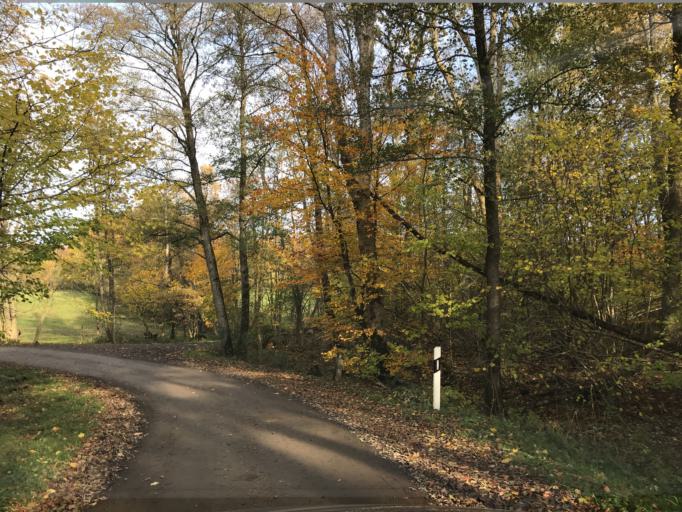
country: SE
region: Skane
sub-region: Bjuvs Kommun
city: Billesholm
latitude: 56.0666
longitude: 13.0196
